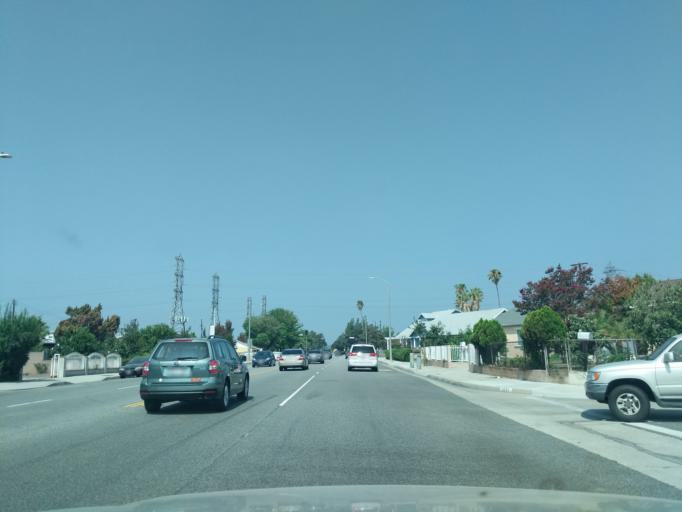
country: US
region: California
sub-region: Los Angeles County
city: Rosemead
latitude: 34.0870
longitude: -118.0802
